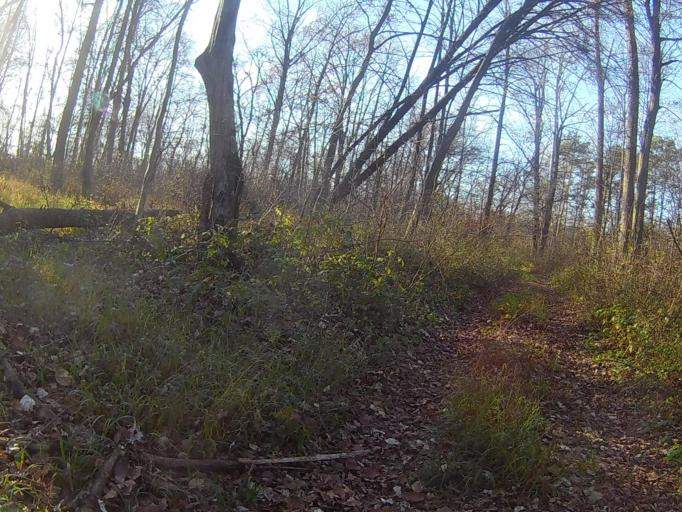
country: SI
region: Duplek
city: Zgornji Duplek
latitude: 46.5104
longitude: 15.7197
